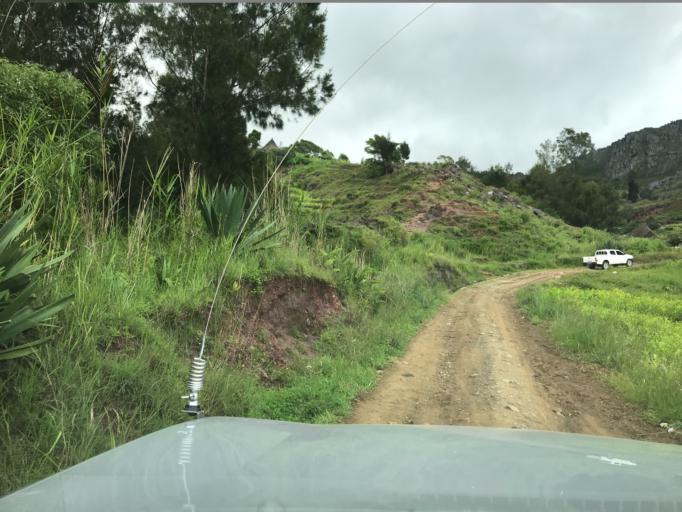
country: TL
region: Aileu
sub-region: Aileu Villa
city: Aileu
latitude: -8.8617
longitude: 125.5693
